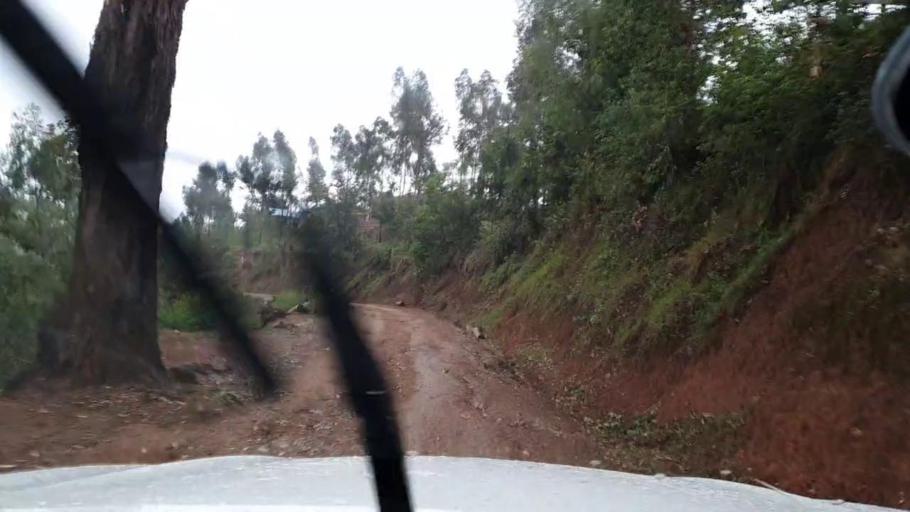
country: BI
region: Kayanza
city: Kayanza
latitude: -2.7846
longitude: 29.5324
